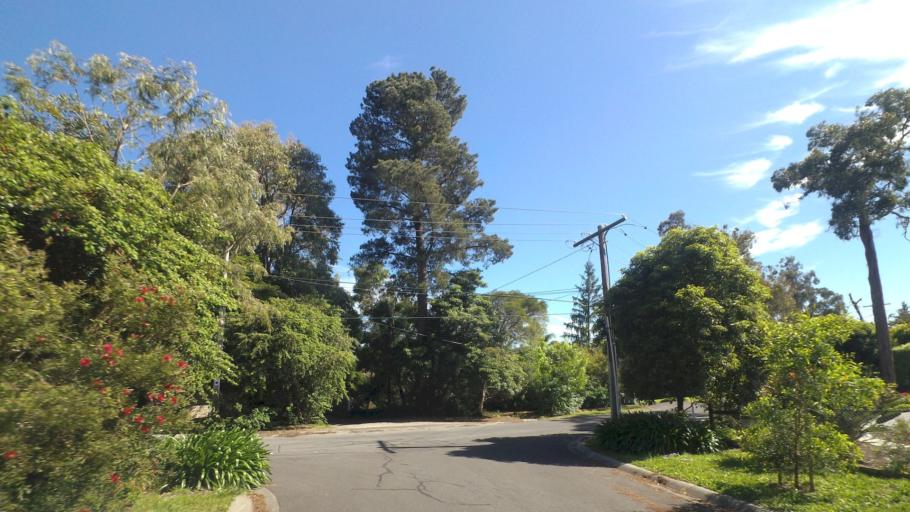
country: AU
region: Victoria
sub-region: Maroondah
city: Ringwood East
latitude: -37.8206
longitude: 145.2520
